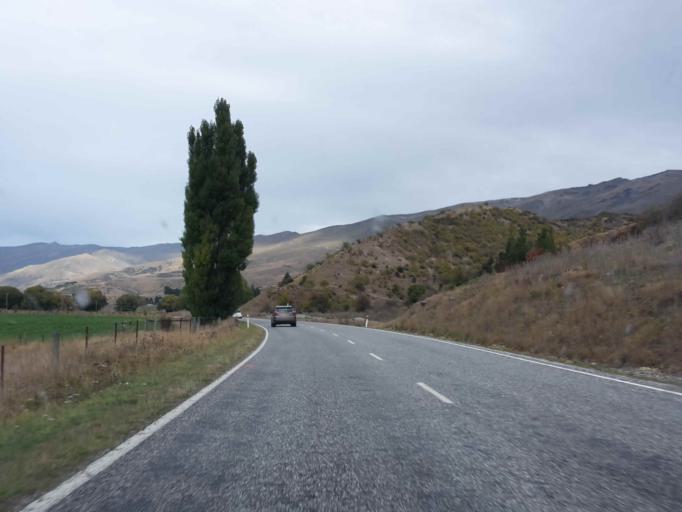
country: NZ
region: Otago
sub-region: Queenstown-Lakes District
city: Wanaka
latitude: -44.8503
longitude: 169.0401
